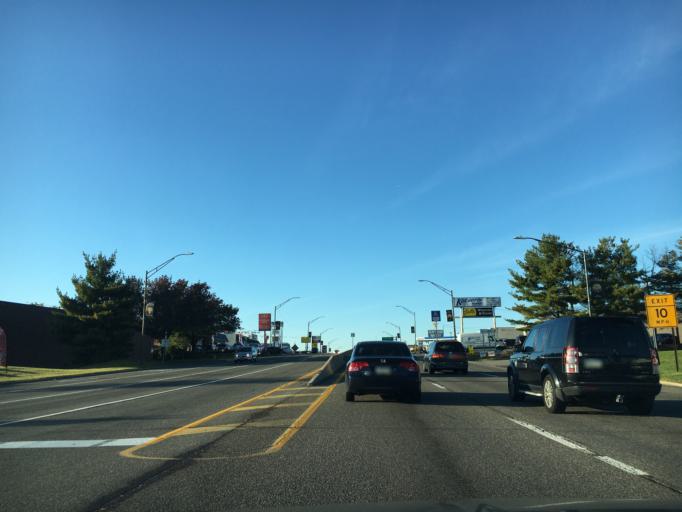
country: US
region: Pennsylvania
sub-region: Lehigh County
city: Fullerton
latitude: 40.6377
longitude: -75.4885
